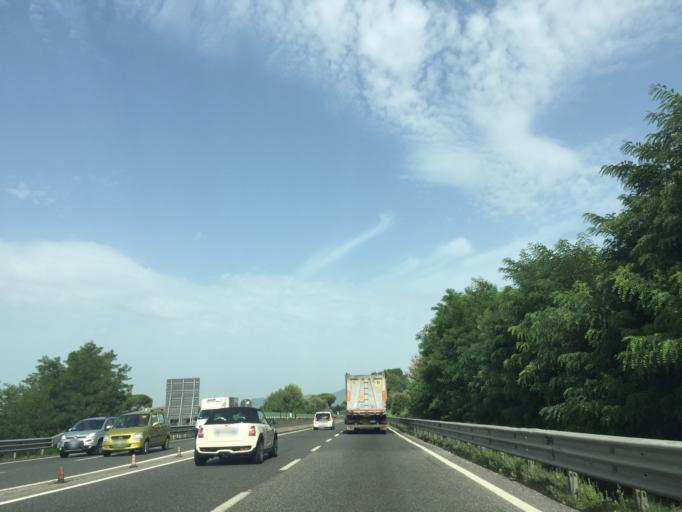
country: IT
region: Tuscany
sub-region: Province of Florence
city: San Pierino
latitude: 43.6978
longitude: 10.8225
